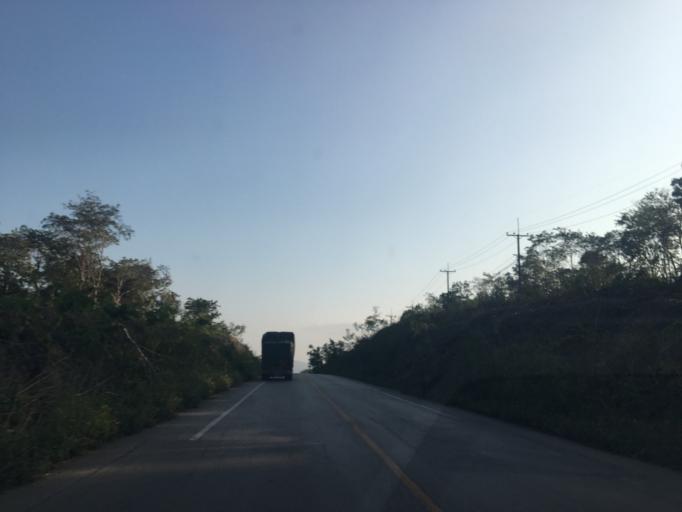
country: TH
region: Lampang
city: Ngao
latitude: 18.6514
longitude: 100.0177
